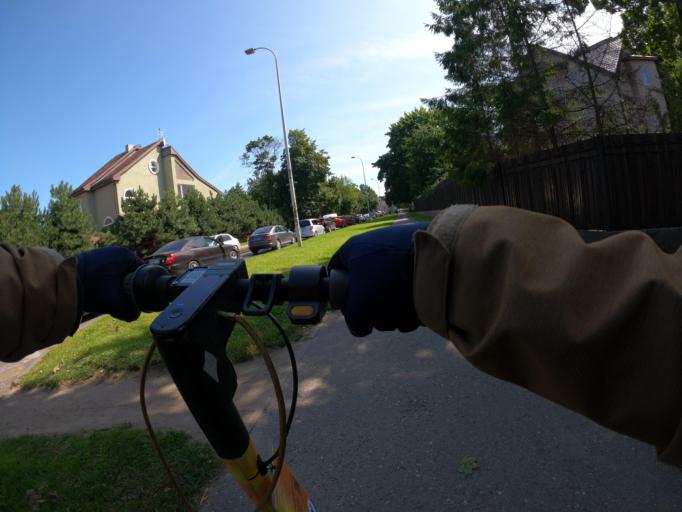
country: RU
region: Kaliningrad
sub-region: Gorod Kaliningrad
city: Kaliningrad
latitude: 54.7343
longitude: 20.5291
